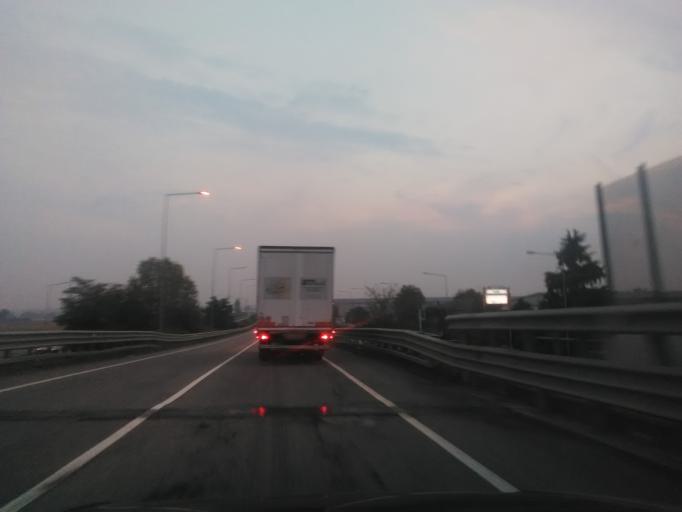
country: IT
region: Piedmont
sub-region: Provincia di Vercelli
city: Carisio
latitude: 45.4339
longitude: 8.2194
